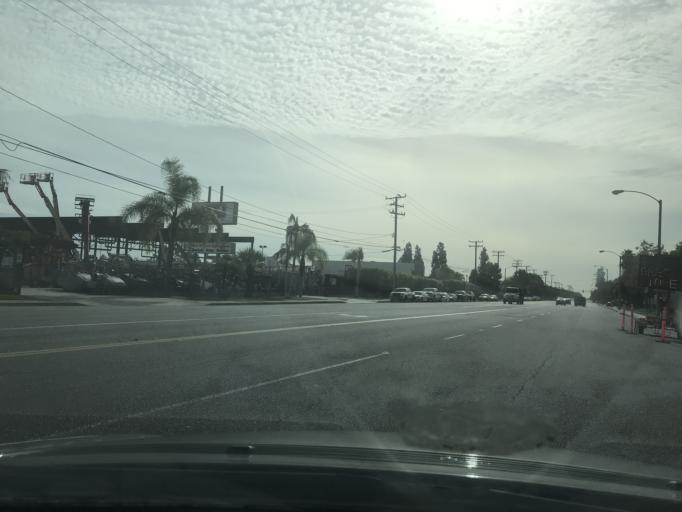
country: US
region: California
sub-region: Los Angeles County
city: South Whittier
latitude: 33.9350
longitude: -118.0556
